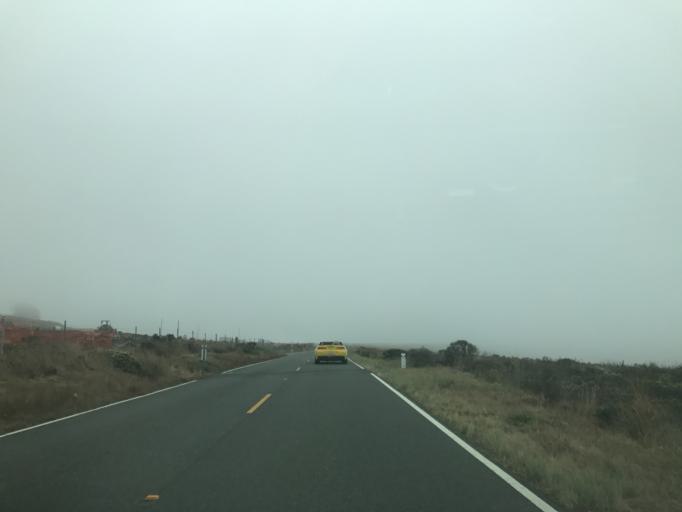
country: US
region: California
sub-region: Sonoma County
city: Monte Rio
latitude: 38.4603
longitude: -123.1439
